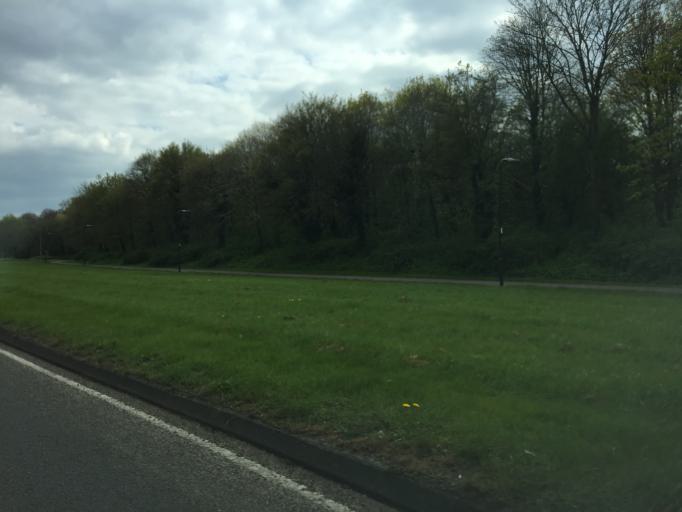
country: GB
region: England
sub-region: Milton Keynes
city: Milton Keynes
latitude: 52.0677
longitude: -0.7631
